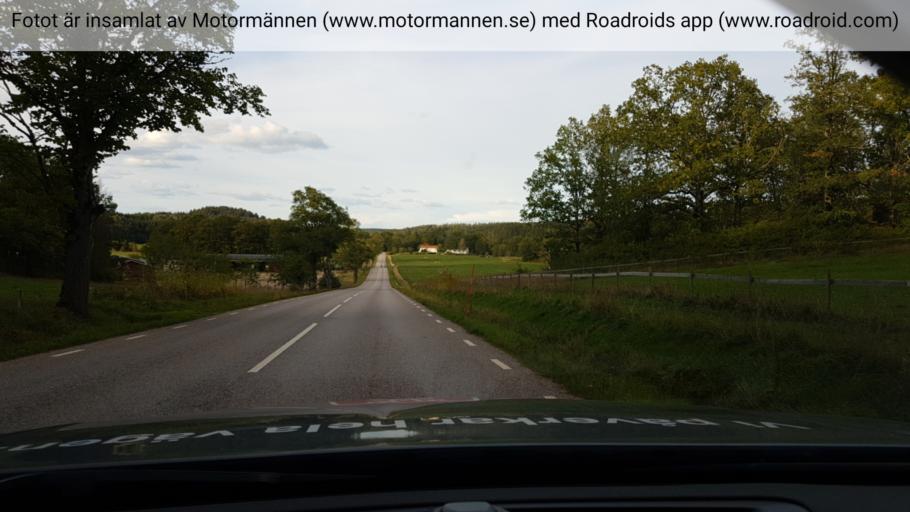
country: SE
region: Kalmar
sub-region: Vasterviks Kommun
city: Gamleby
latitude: 57.9102
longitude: 16.4112
